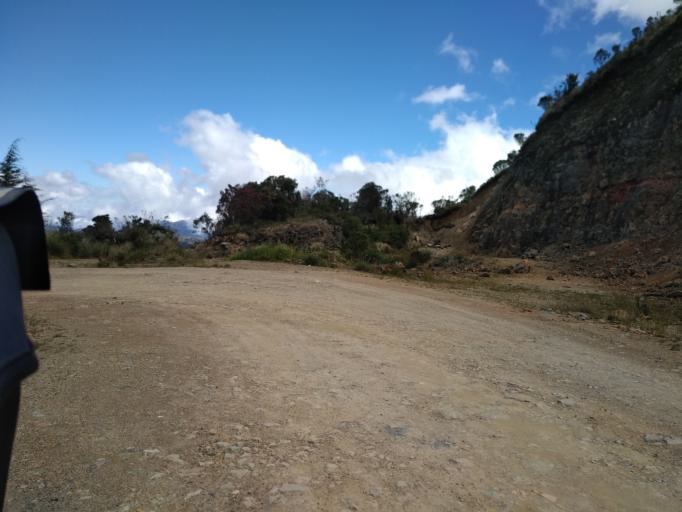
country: CO
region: Boyaca
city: Duitama
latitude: 5.9376
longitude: -73.1044
